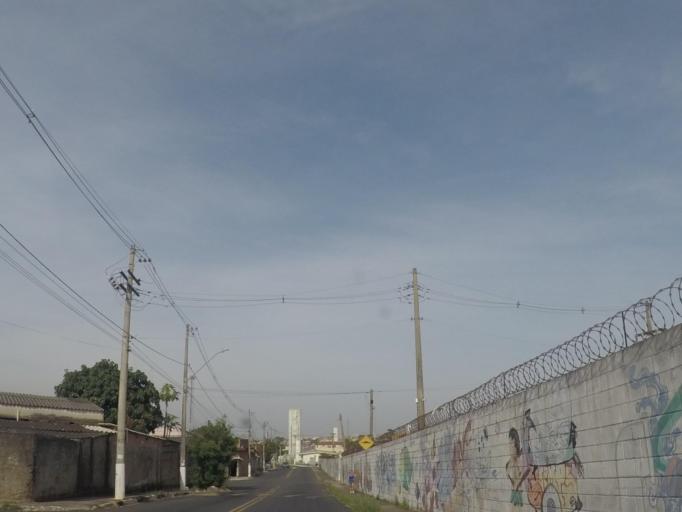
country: BR
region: Sao Paulo
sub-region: Hortolandia
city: Hortolandia
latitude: -22.8491
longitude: -47.2000
